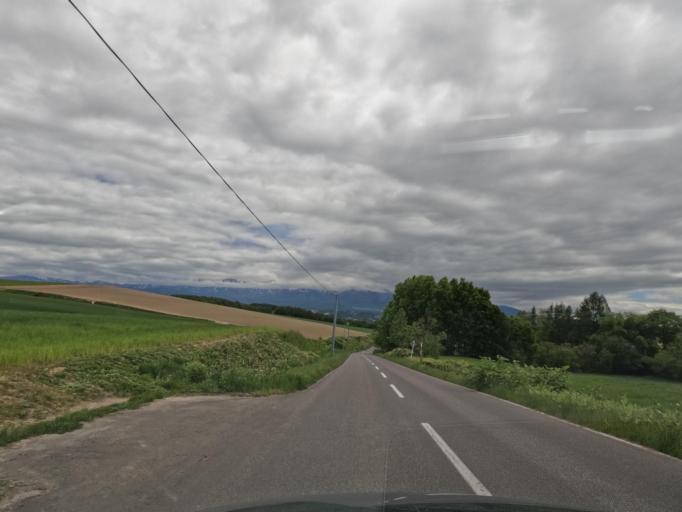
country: JP
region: Hokkaido
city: Shimo-furano
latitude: 43.4887
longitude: 142.4199
